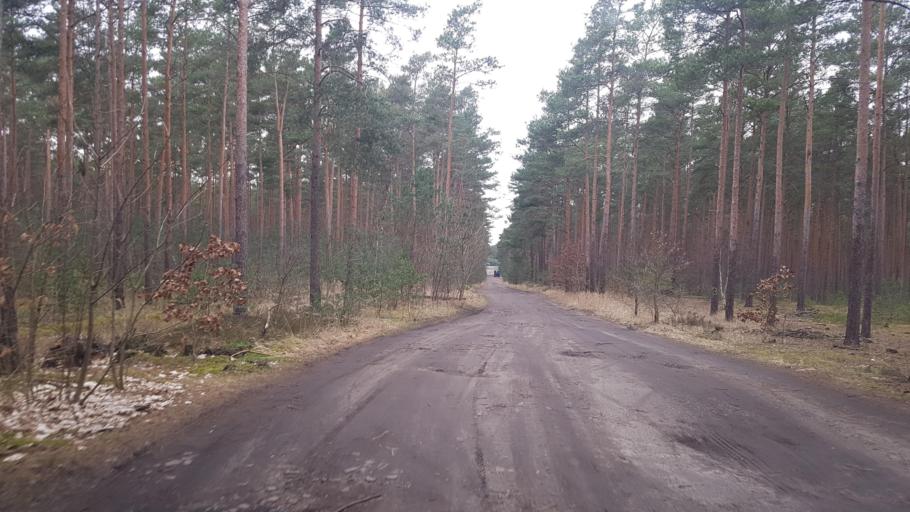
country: DE
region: Brandenburg
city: Halbe
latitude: 52.0633
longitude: 13.6631
